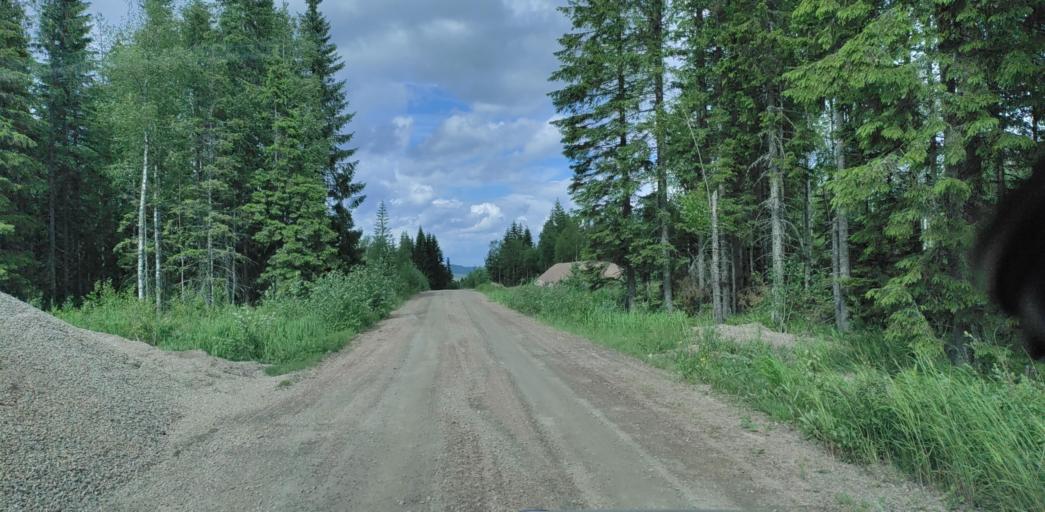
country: SE
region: Vaermland
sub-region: Munkfors Kommun
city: Munkfors
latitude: 59.9554
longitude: 13.4108
